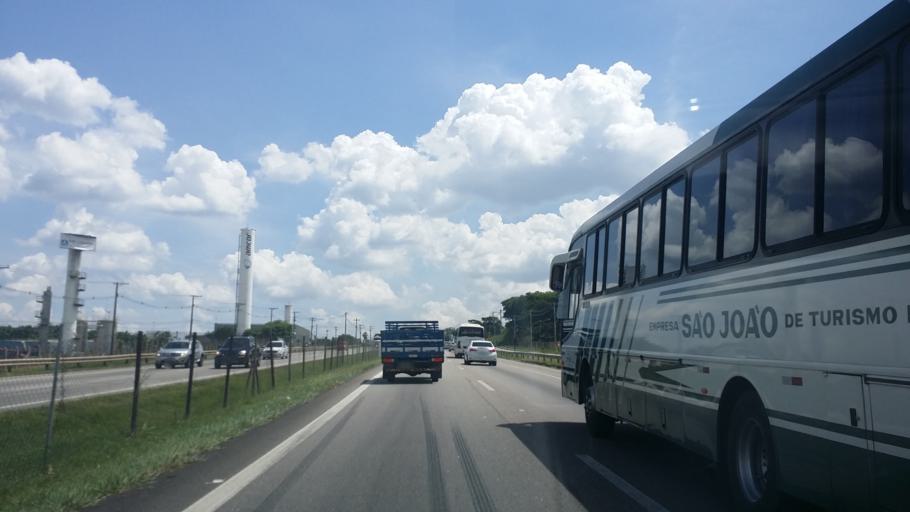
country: BR
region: Sao Paulo
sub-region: Jundiai
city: Jundiai
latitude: -23.1767
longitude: -46.9549
